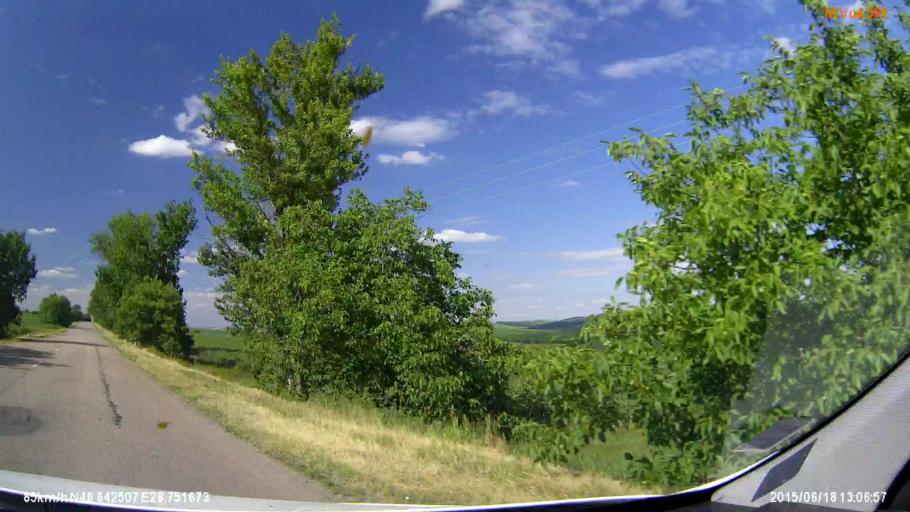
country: MD
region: Cimislia
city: Cimislia
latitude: 46.6423
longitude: 28.7517
